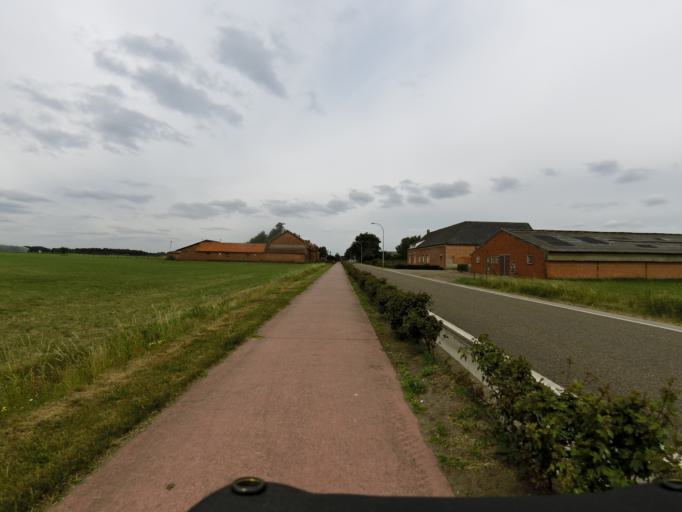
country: NL
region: North Brabant
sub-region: Gemeente Goirle
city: Goirle
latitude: 51.4354
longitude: 5.0679
